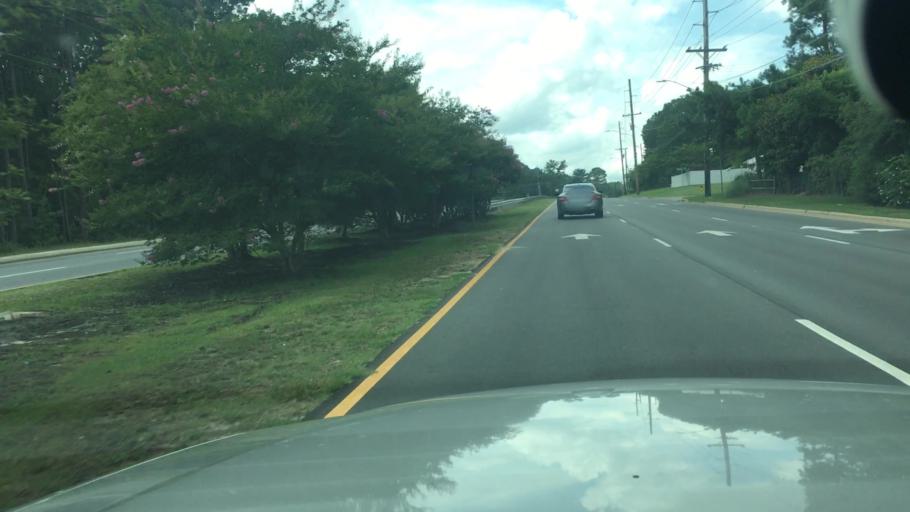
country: US
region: North Carolina
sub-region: Cumberland County
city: Fayetteville
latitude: 35.0695
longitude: -78.9137
